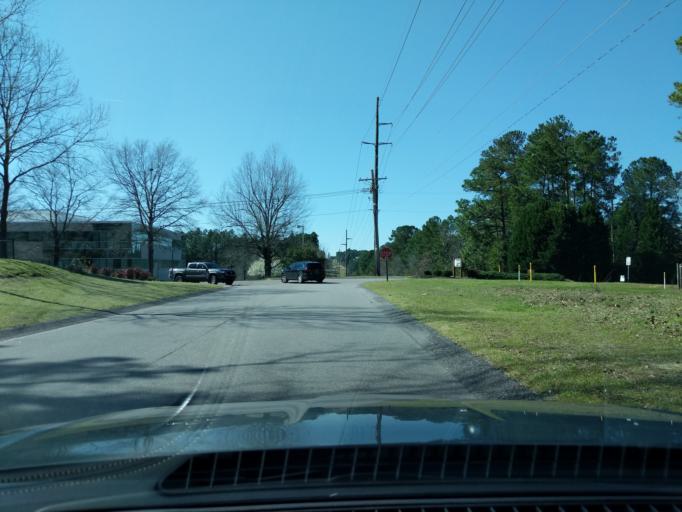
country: US
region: South Carolina
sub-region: Aiken County
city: Aiken
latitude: 33.5323
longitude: -81.7514
